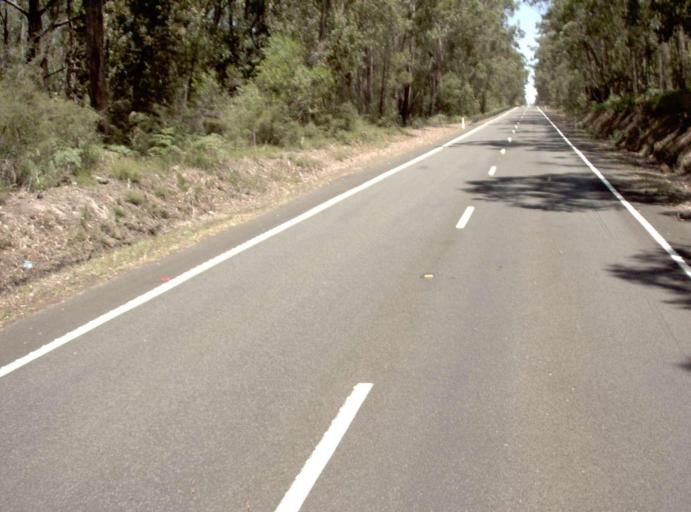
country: AU
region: Victoria
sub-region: East Gippsland
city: Lakes Entrance
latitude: -37.7411
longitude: 148.0778
